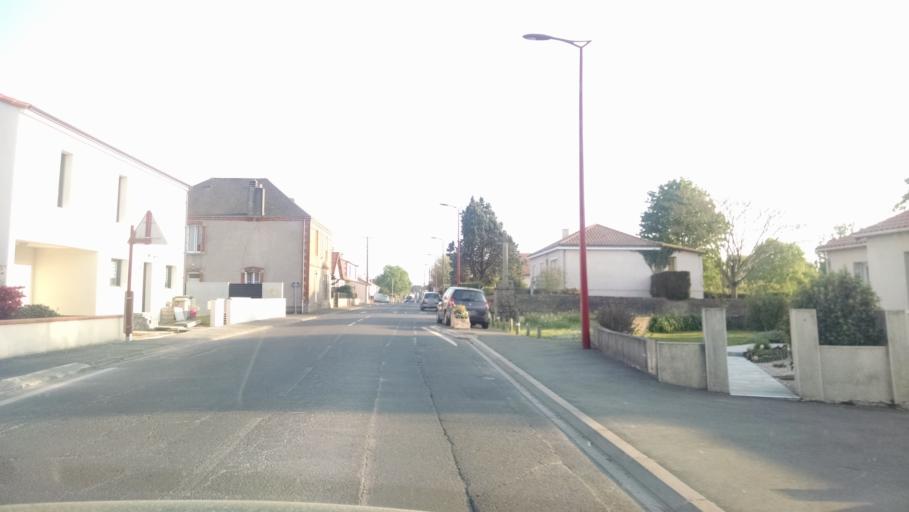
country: FR
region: Pays de la Loire
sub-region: Departement de la Loire-Atlantique
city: Boussay
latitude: 47.0496
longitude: -1.1845
